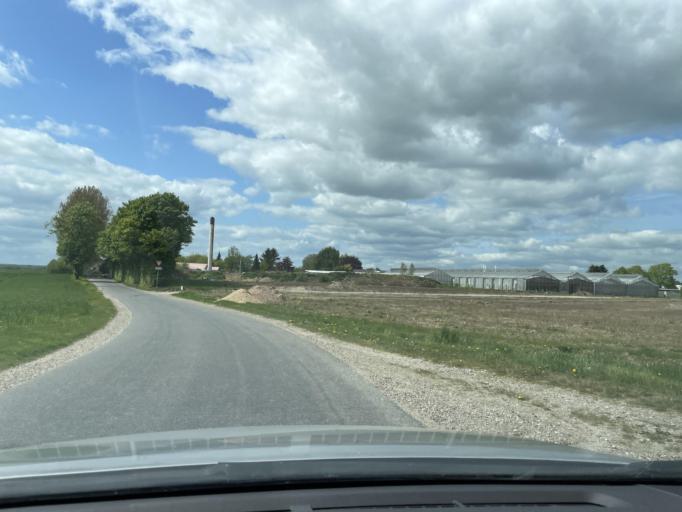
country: DK
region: Central Jutland
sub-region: Skanderborg Kommune
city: Skanderborg
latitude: 55.9279
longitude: 9.9509
